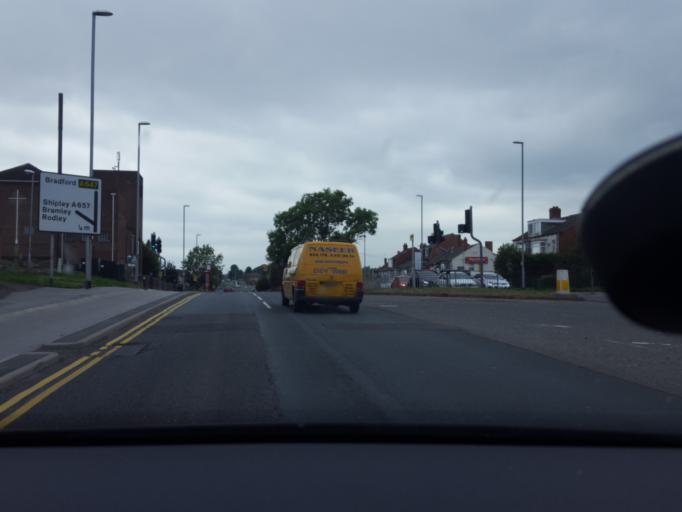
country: GB
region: England
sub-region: City and Borough of Leeds
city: Horsforth
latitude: 53.8036
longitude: -1.6119
